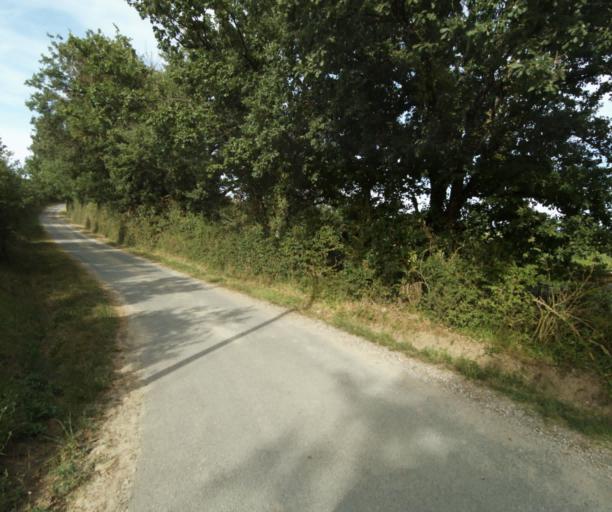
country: FR
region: Midi-Pyrenees
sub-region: Departement du Tarn
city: Puylaurens
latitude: 43.5346
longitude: 2.0478
